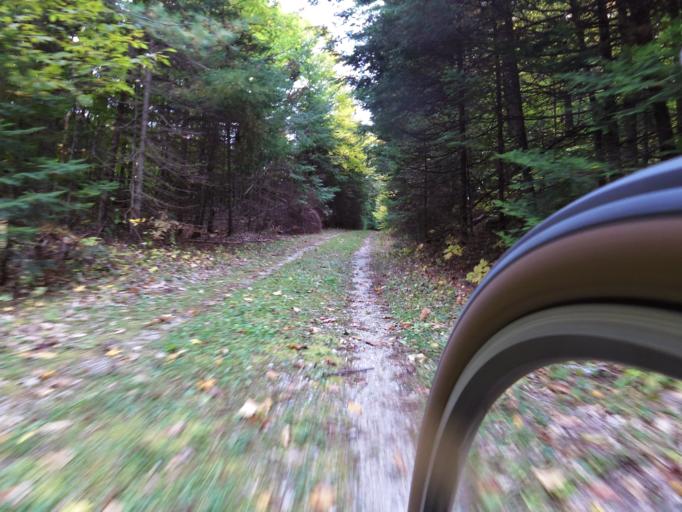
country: CA
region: Quebec
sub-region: Outaouais
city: Wakefield
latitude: 45.6008
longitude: -76.0651
